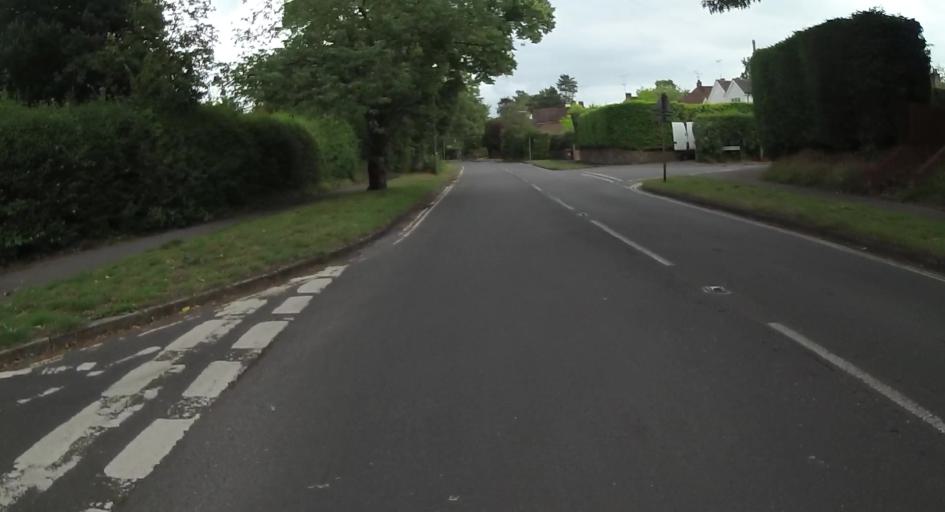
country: GB
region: England
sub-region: Surrey
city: Farnham
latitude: 51.2116
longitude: -0.7864
